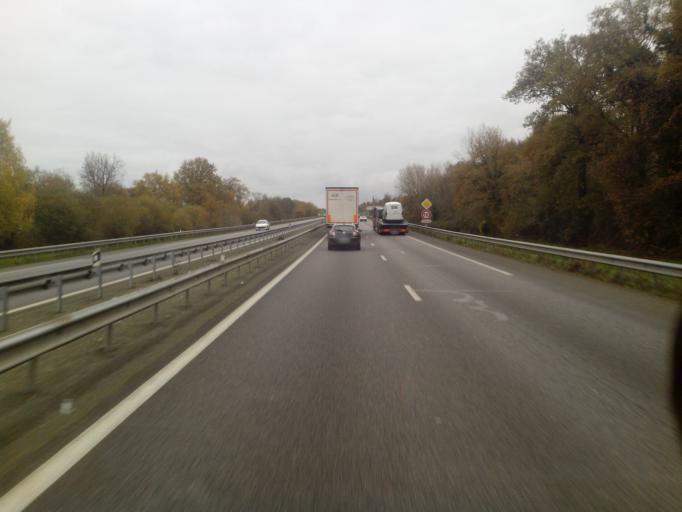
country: FR
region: Brittany
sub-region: Departement d'Ille-et-Vilaine
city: Laille
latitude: 47.9871
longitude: -1.6955
